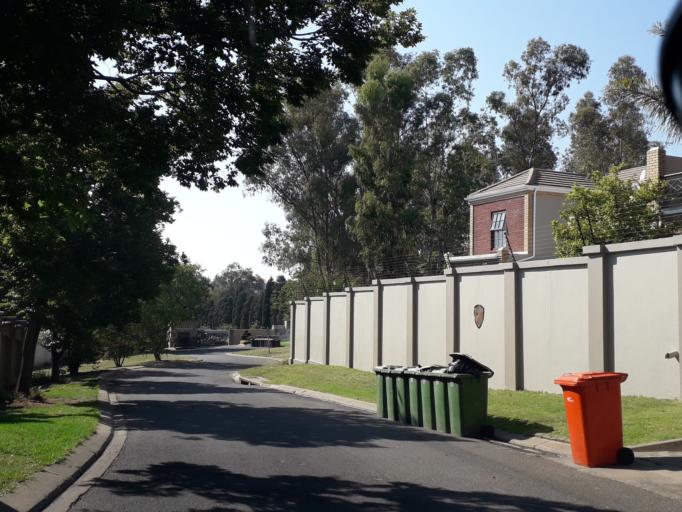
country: ZA
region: Gauteng
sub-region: City of Johannesburg Metropolitan Municipality
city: Midrand
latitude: -26.0349
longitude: 28.0528
